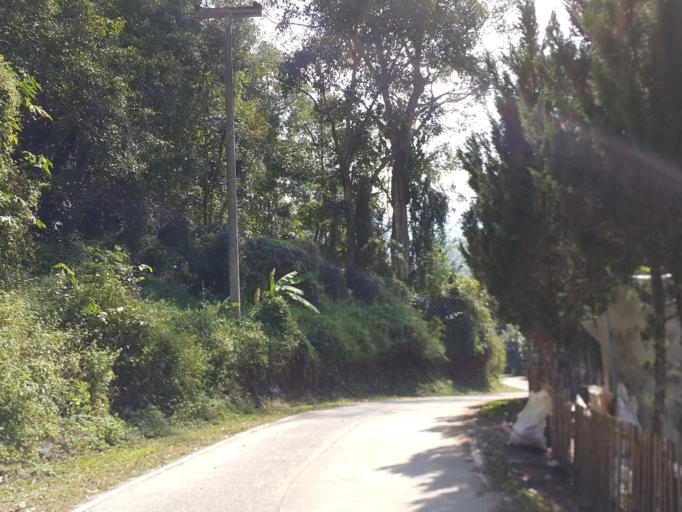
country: TH
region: Lampang
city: Wang Nuea
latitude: 19.0628
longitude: 99.3618
